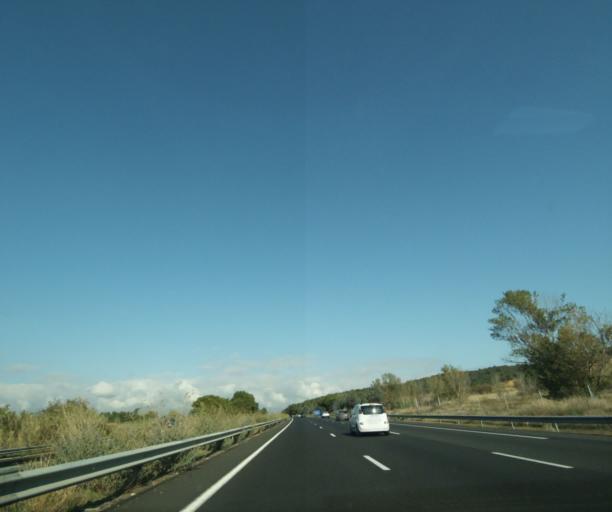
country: FR
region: Languedoc-Roussillon
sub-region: Departement de l'Aude
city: Vinassan
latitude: 43.1966
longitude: 3.0754
